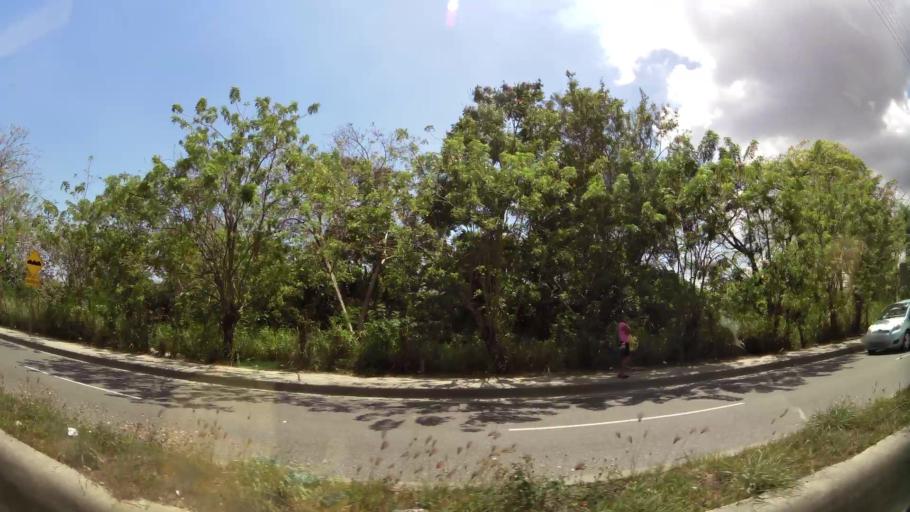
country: DO
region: Nacional
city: Santo Domingo
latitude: 18.5091
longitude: -69.9648
